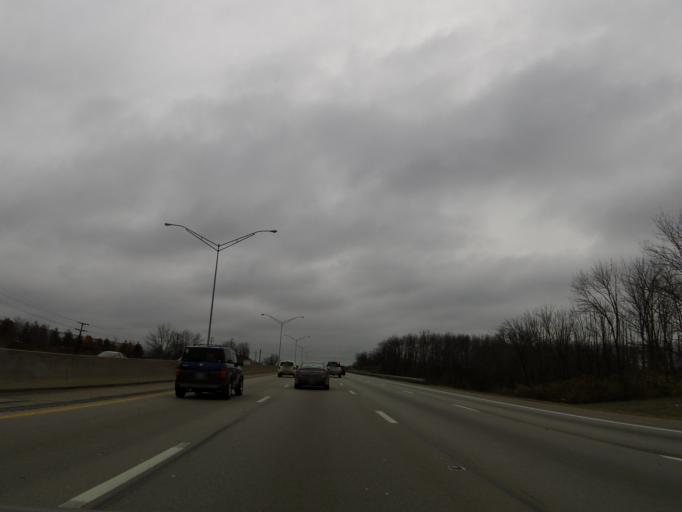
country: US
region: Kentucky
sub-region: Boone County
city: Walton
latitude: 38.9008
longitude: -84.6274
